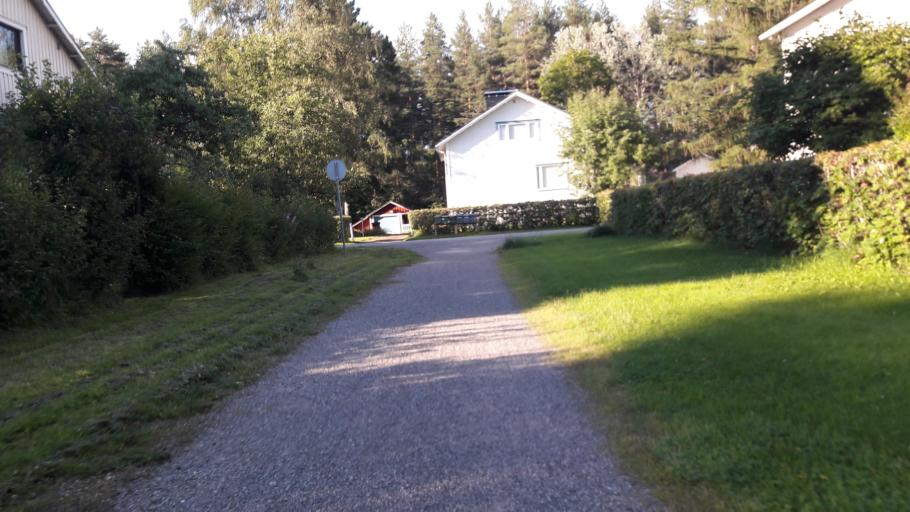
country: FI
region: North Karelia
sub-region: Joensuu
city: Joensuu
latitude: 62.6098
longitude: 29.7532
